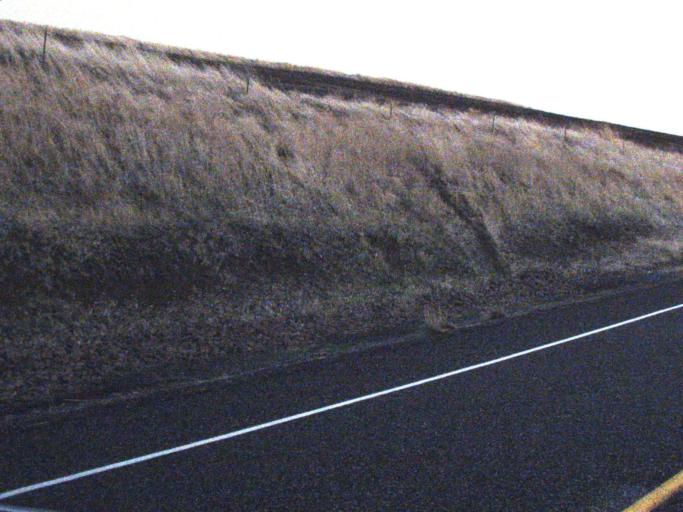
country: US
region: Washington
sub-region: Garfield County
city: Pomeroy
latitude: 46.5462
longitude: -117.7752
